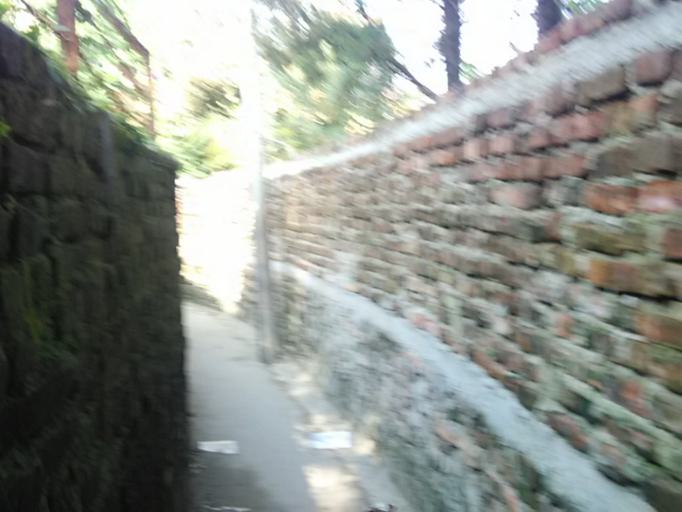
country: NP
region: Central Region
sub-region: Bagmati Zone
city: Kathmandu
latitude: 27.7350
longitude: 85.3417
